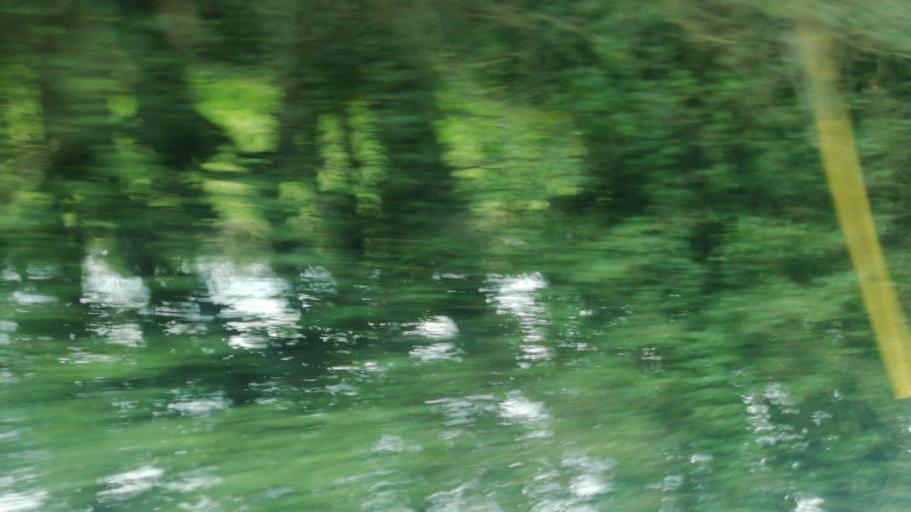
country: IE
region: Leinster
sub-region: Kildare
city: Clane
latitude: 53.3097
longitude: -6.7195
